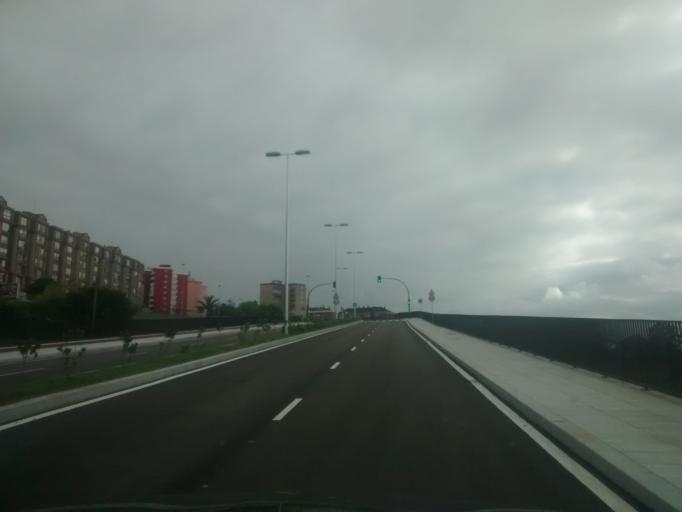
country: ES
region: Cantabria
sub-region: Provincia de Cantabria
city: Santander
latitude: 43.4686
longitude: -3.8185
